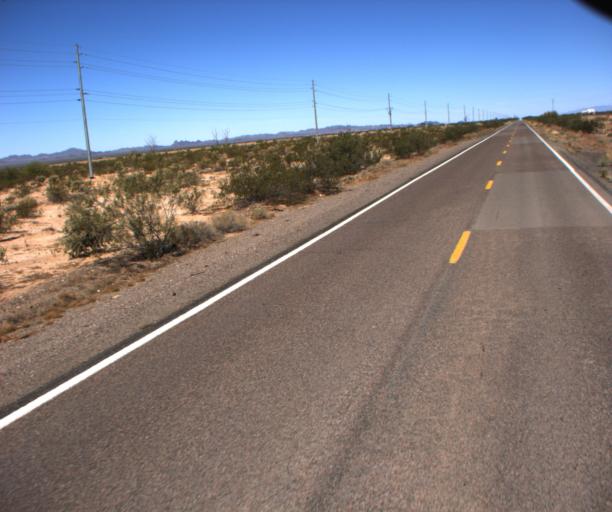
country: US
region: Arizona
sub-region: La Paz County
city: Salome
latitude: 33.8354
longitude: -113.8826
